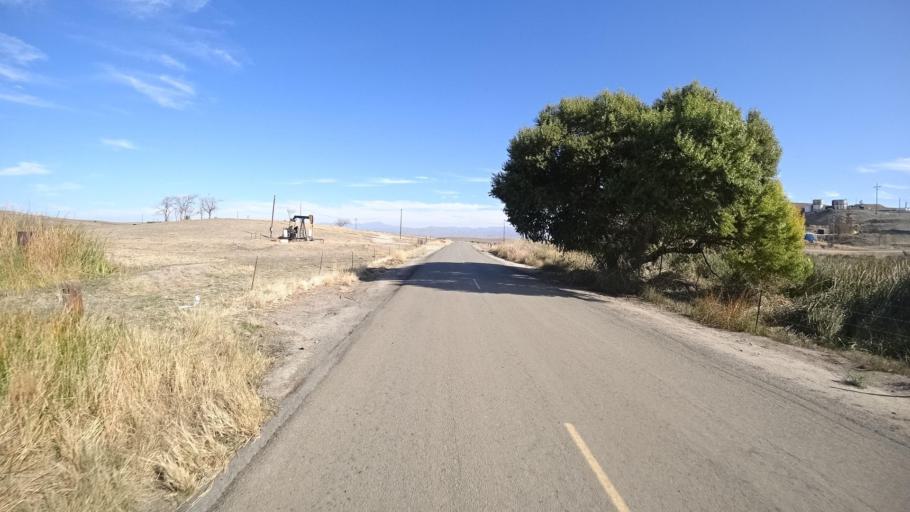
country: US
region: California
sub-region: Tulare County
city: Richgrove
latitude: 35.6327
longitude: -118.9603
